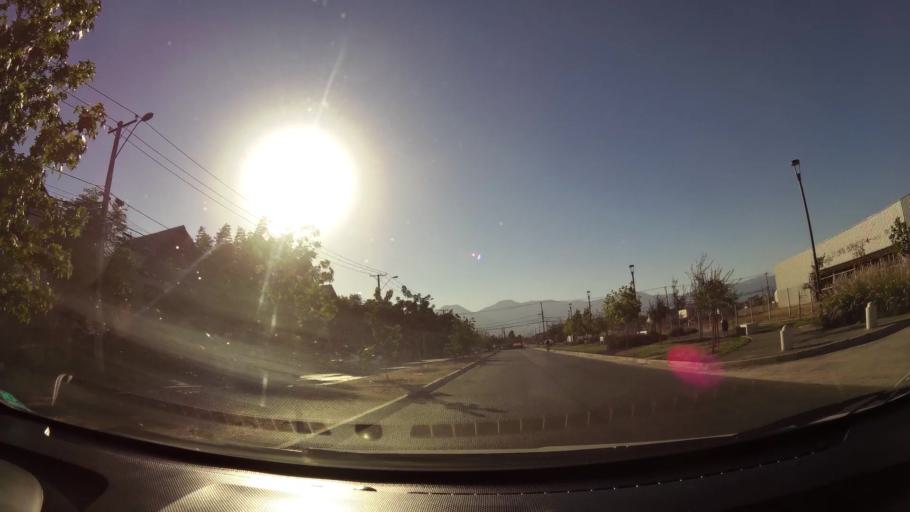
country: CL
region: O'Higgins
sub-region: Provincia de Cachapoal
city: Rancagua
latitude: -34.1815
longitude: -70.7630
